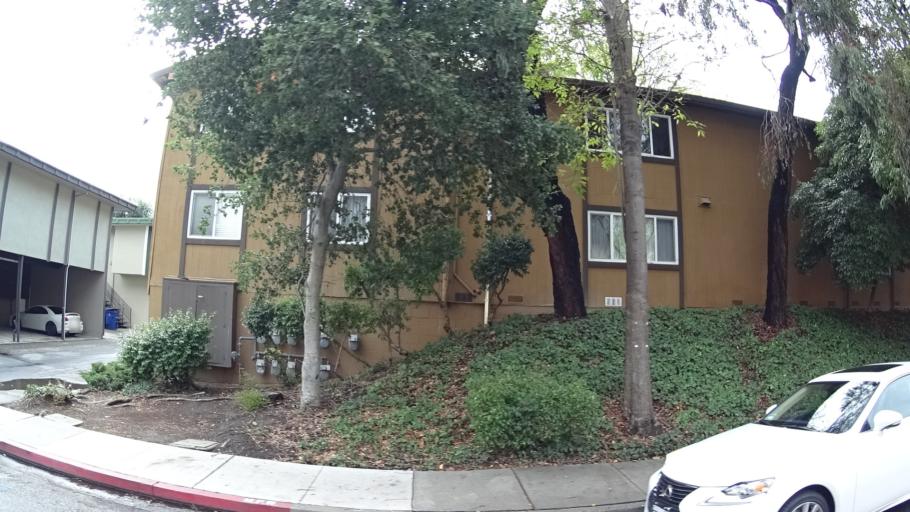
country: US
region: California
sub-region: San Mateo County
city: Millbrae
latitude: 37.6012
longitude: -122.4004
